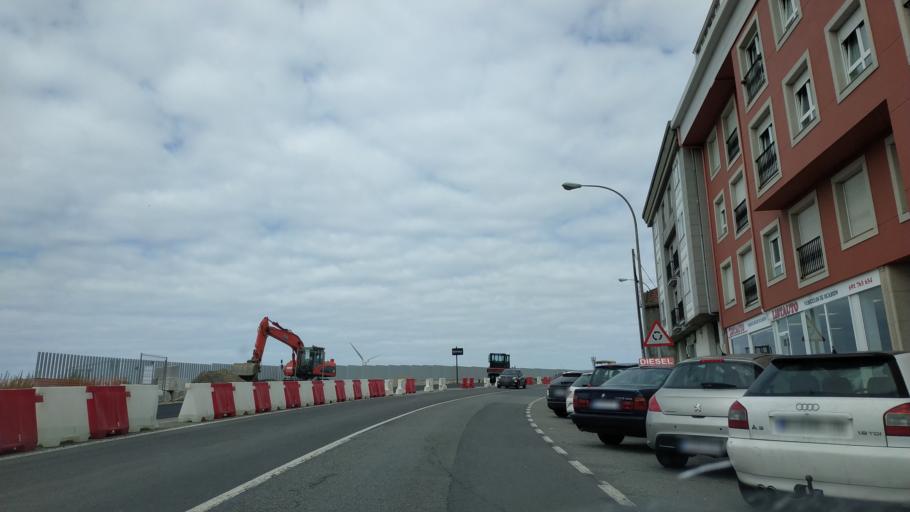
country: ES
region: Galicia
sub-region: Provincia da Coruna
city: Arteixo
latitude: 43.3128
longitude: -8.5012
